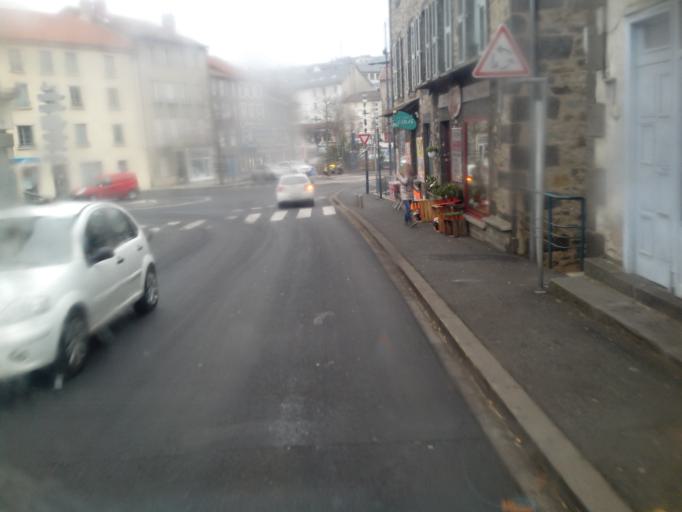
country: FR
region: Auvergne
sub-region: Departement du Cantal
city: Saint-Flour
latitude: 45.0330
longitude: 3.1005
